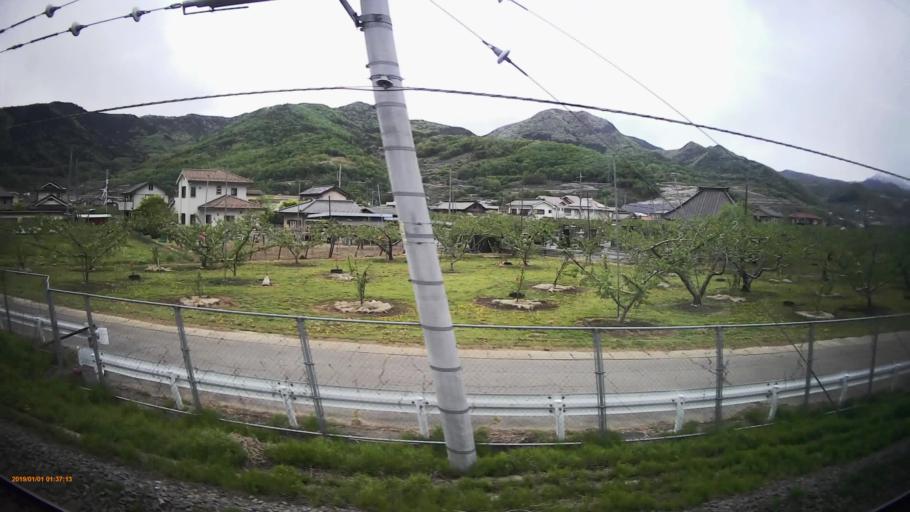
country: JP
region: Yamanashi
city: Isawa
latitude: 35.6686
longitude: 138.6528
